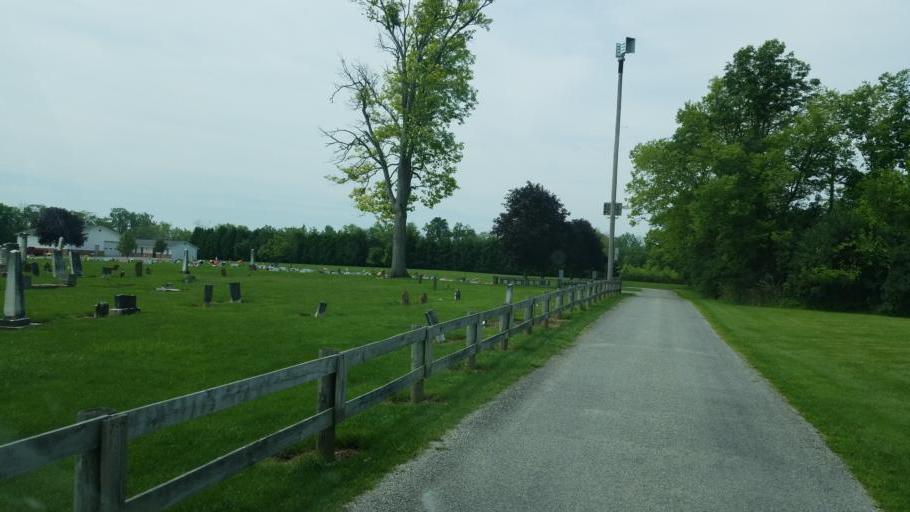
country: US
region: Ohio
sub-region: Madison County
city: West Jefferson
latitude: 39.9403
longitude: -83.2694
